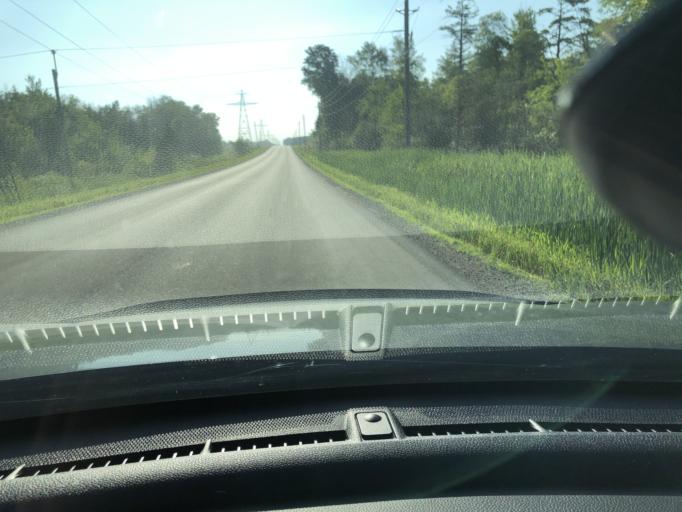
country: CA
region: Ontario
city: Stratford
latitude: 43.3882
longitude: -80.8657
